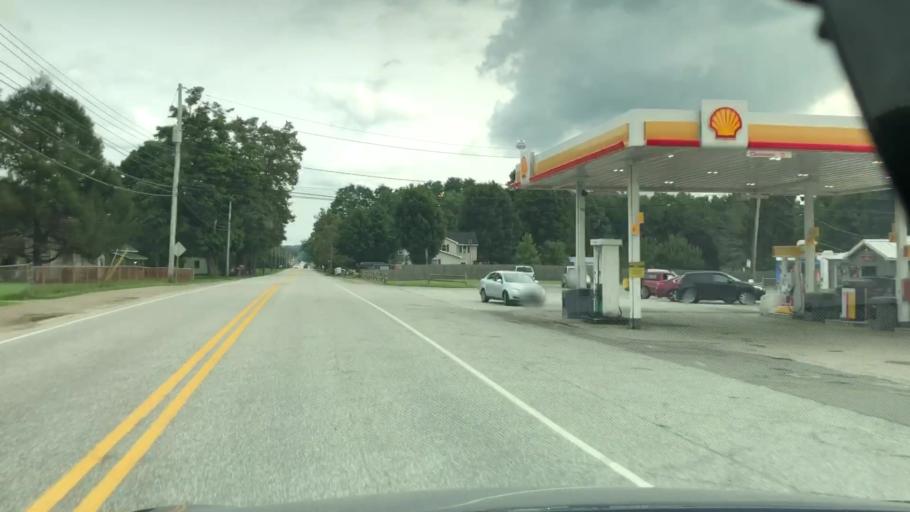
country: US
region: Pennsylvania
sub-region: Erie County
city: Union City
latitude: 42.0235
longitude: -79.8180
